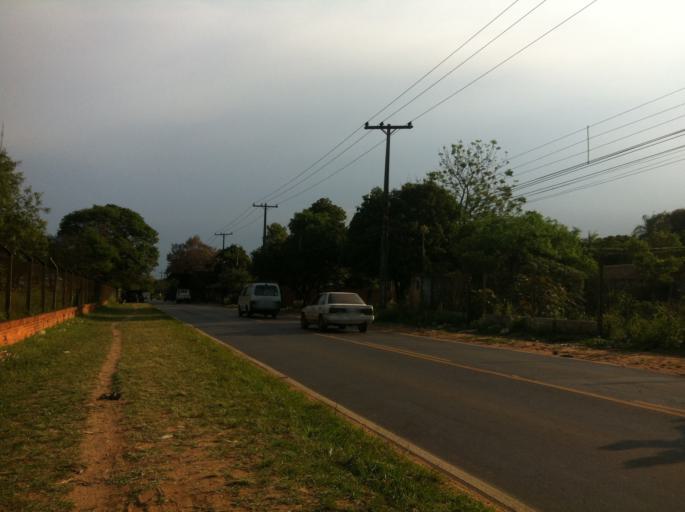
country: PY
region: Central
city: San Lorenzo
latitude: -25.2937
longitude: -57.4914
